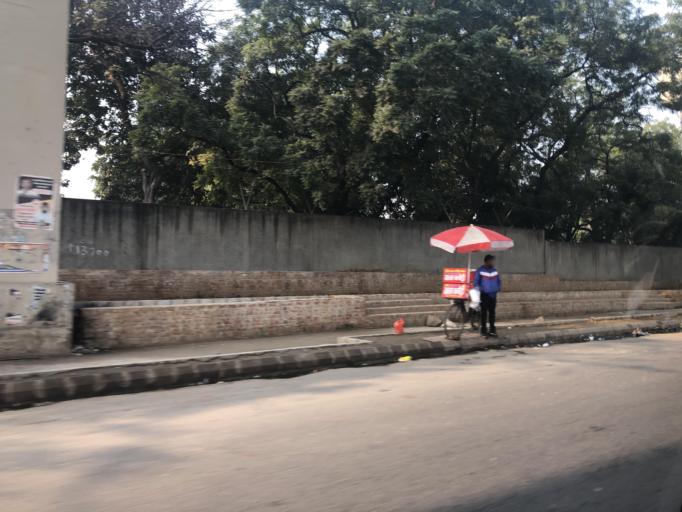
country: IN
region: NCT
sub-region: Central Delhi
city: Karol Bagh
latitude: 28.6000
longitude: 77.1615
